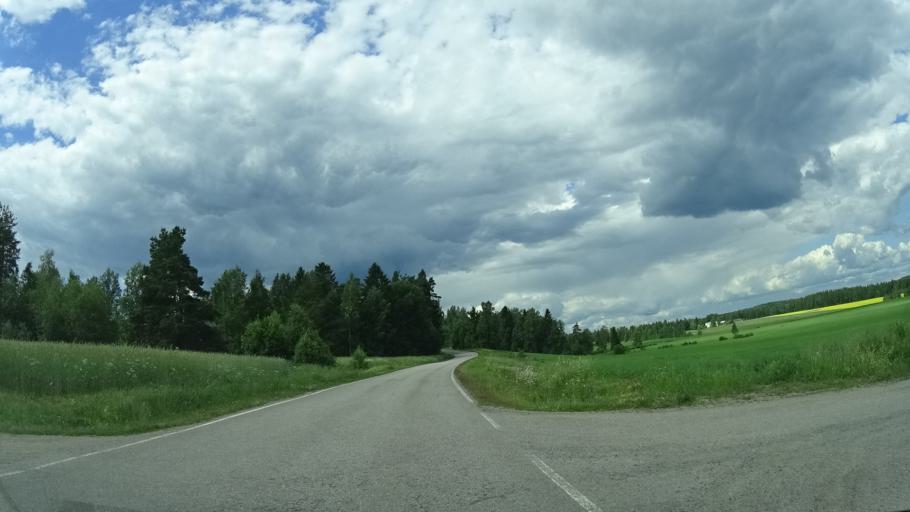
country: FI
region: Uusimaa
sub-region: Helsinki
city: Espoo
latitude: 60.4111
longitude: 24.5725
